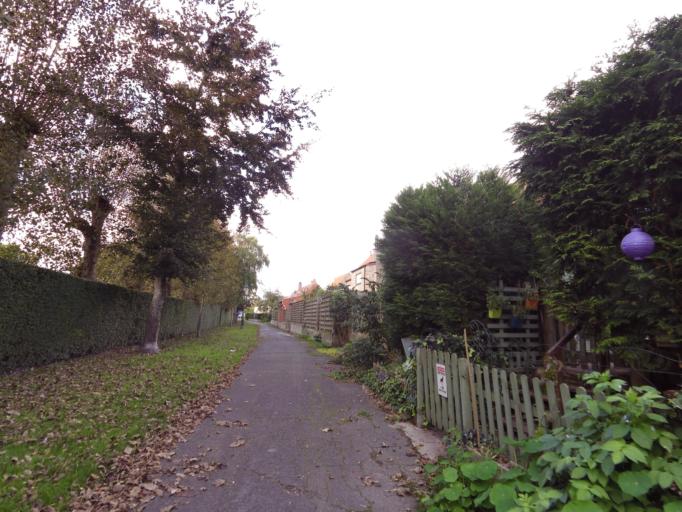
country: BE
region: Flanders
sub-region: Provincie West-Vlaanderen
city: Ostend
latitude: 51.2018
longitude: 2.9162
